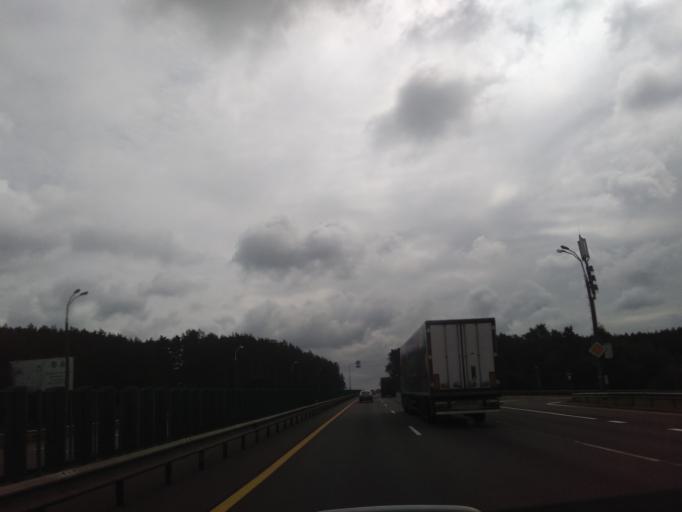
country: BY
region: Minsk
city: Bal'shavik
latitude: 53.9686
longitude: 27.6019
